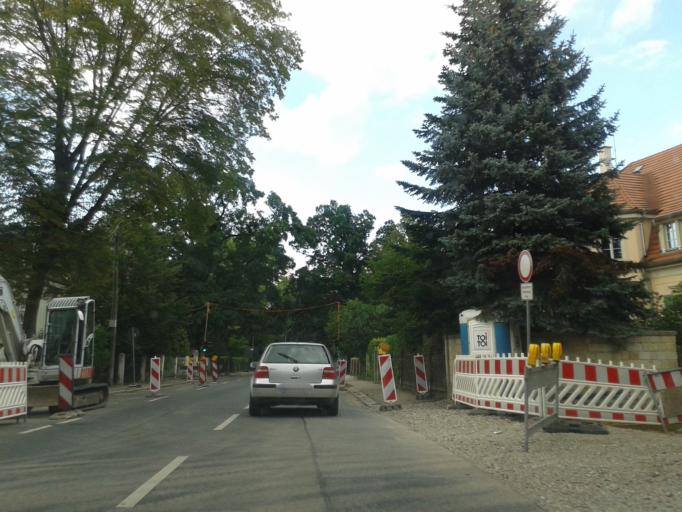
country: DE
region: Saxony
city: Albertstadt
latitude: 51.0543
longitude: 13.8029
